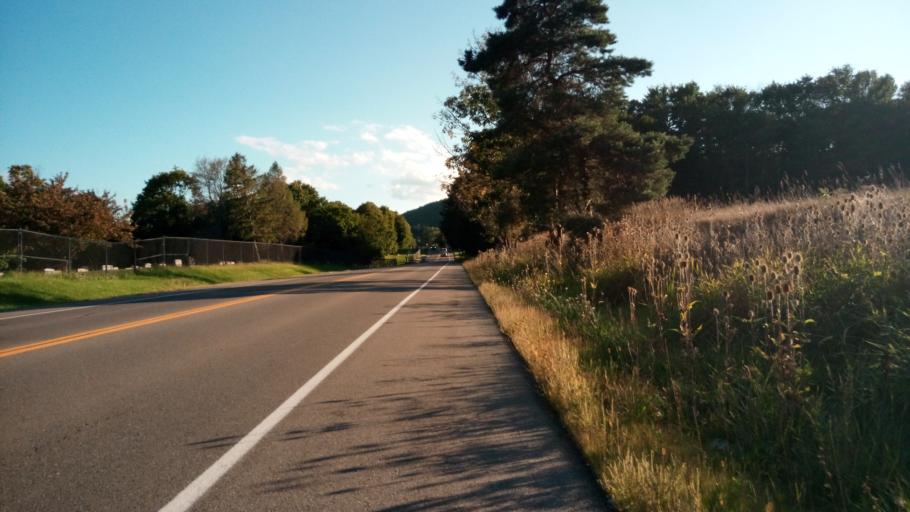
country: US
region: New York
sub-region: Chemung County
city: Elmira Heights
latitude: 42.1099
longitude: -76.8308
